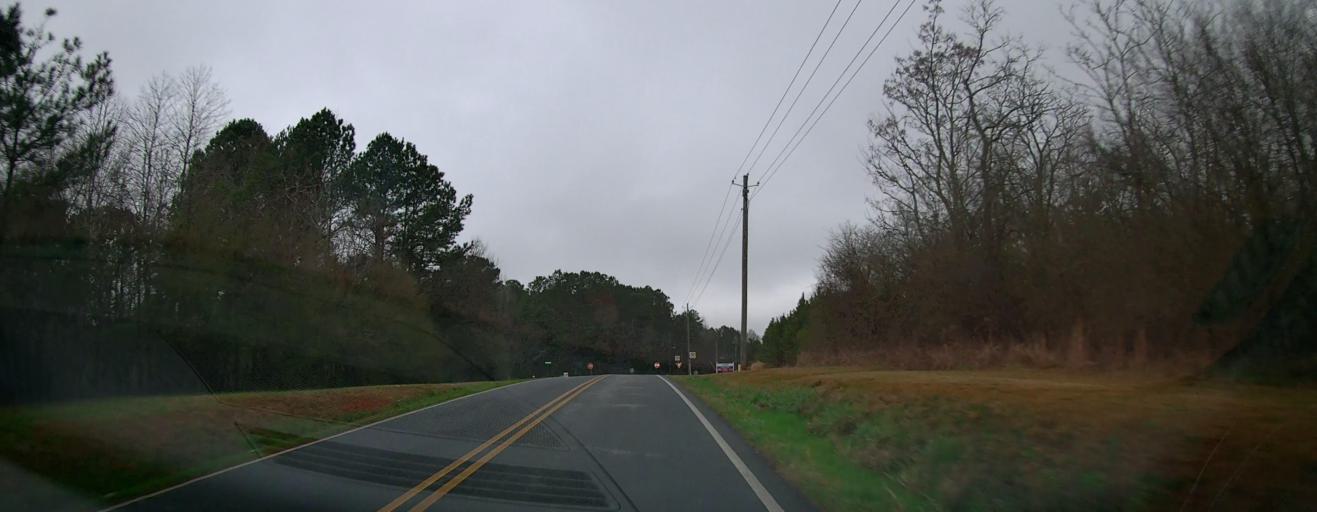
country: US
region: Georgia
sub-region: Pike County
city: Zebulon
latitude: 33.1681
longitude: -84.3606
